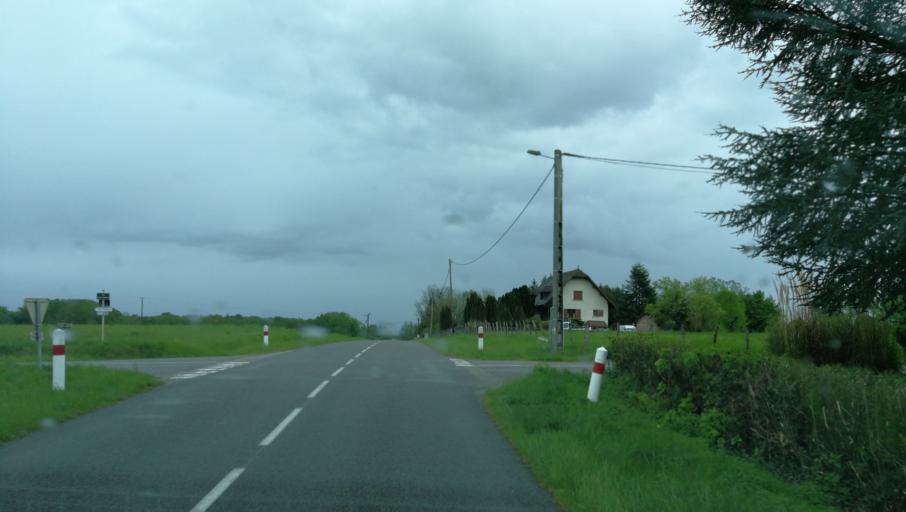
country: FR
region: Franche-Comte
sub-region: Departement du Jura
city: Bletterans
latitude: 46.7898
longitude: 5.4113
